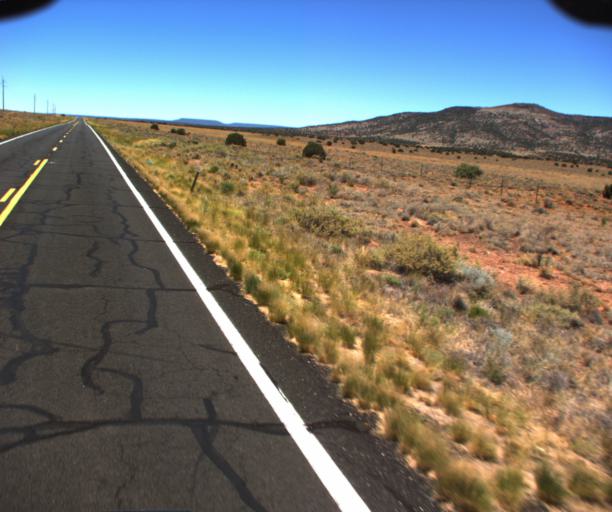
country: US
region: Arizona
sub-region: Coconino County
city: LeChee
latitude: 34.8738
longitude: -110.8961
